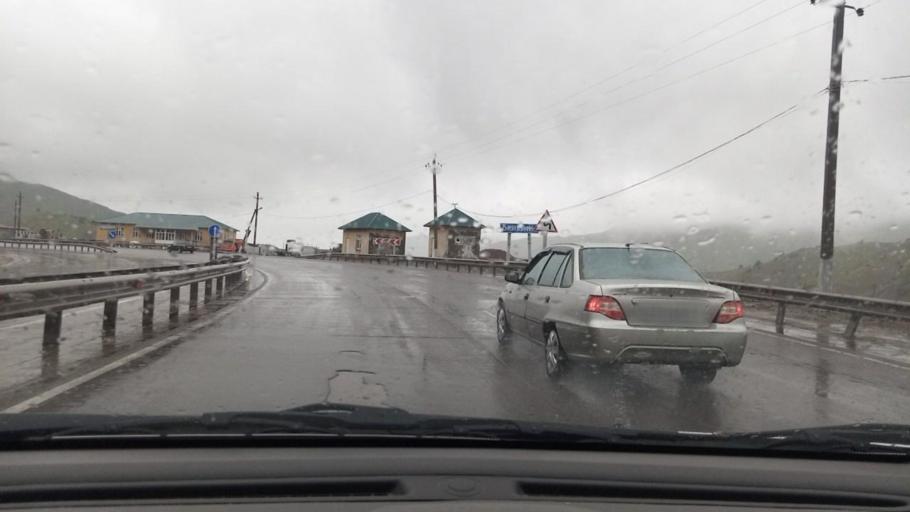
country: UZ
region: Toshkent
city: Angren
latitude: 41.0919
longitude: 70.5318
